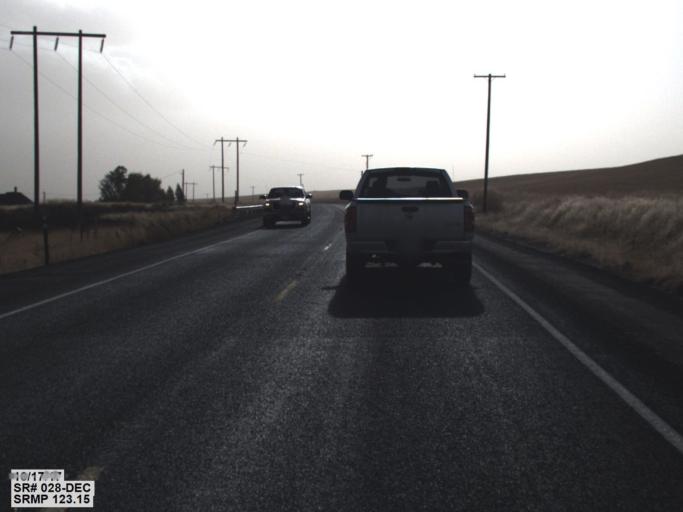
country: US
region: Washington
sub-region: Lincoln County
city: Davenport
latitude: 47.5441
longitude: -118.1917
